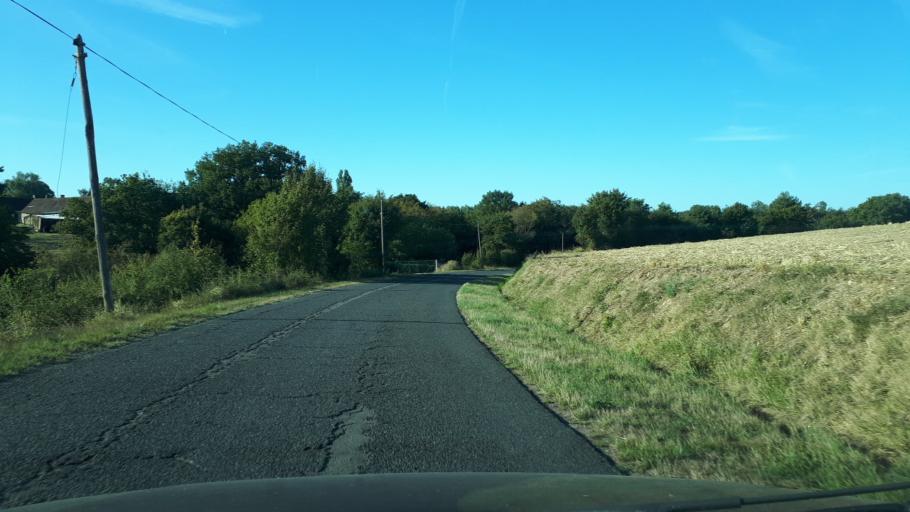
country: FR
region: Centre
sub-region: Departement du Loir-et-Cher
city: Montoire-sur-le-Loir
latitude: 47.7208
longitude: 0.9378
